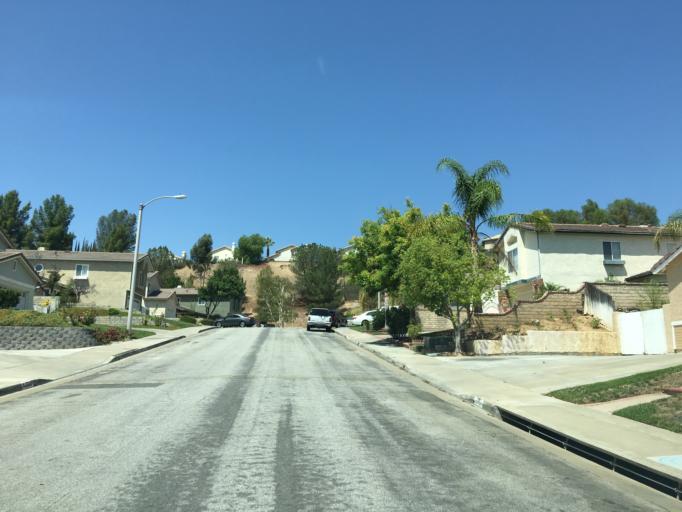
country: US
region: California
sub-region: Los Angeles County
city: Valencia
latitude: 34.4610
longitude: -118.6169
